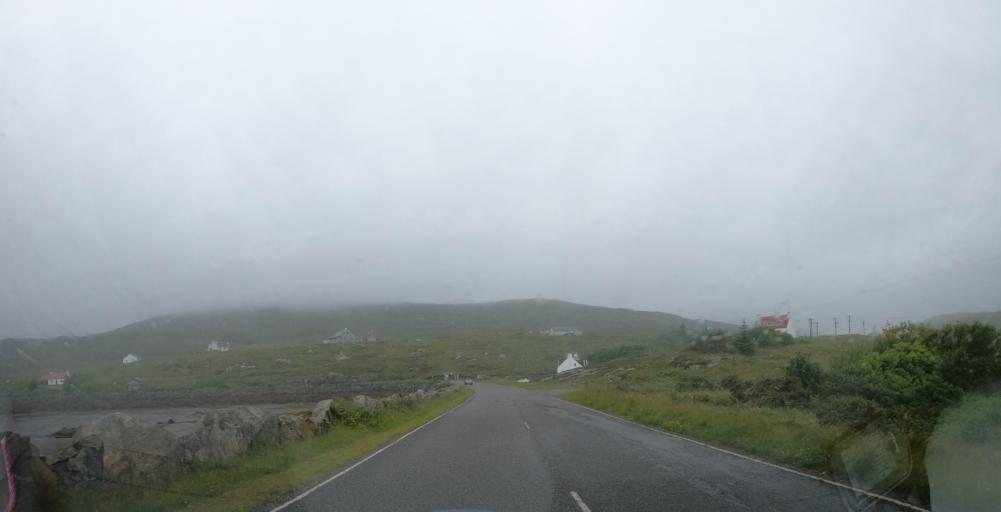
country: GB
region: Scotland
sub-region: Eilean Siar
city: Barra
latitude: 57.0030
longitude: -7.4293
